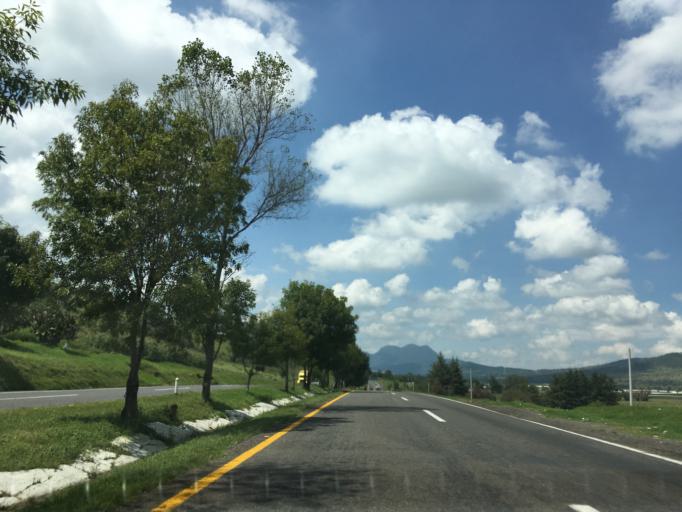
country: MX
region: Michoacan
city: Lagunillas
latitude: 19.5552
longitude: -101.4257
